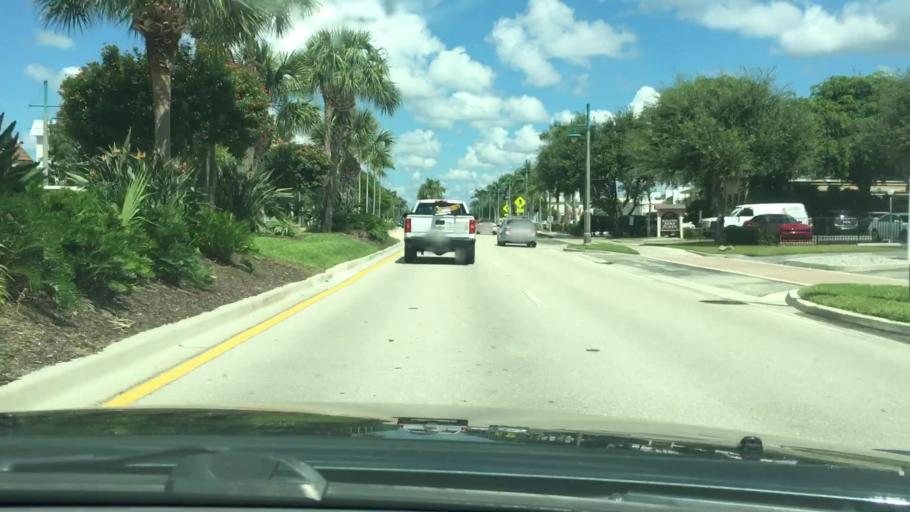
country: US
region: Florida
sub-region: Collier County
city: Marco
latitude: 25.9426
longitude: -81.7325
